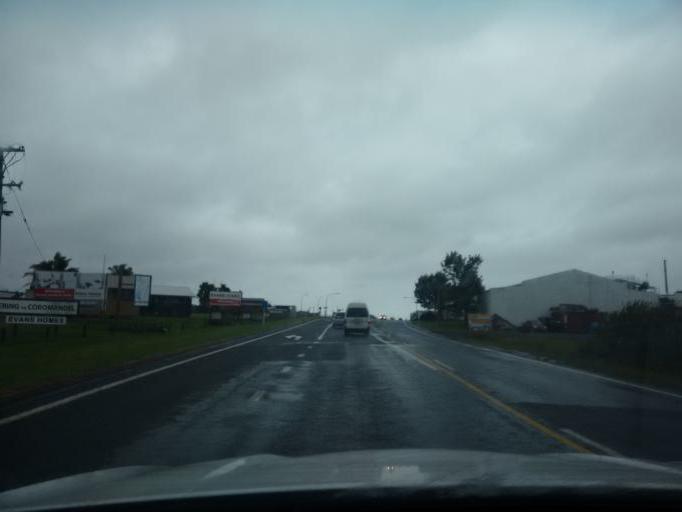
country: NZ
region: Waikato
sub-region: Thames-Coromandel District
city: Whitianga
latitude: -36.8339
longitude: 175.6727
